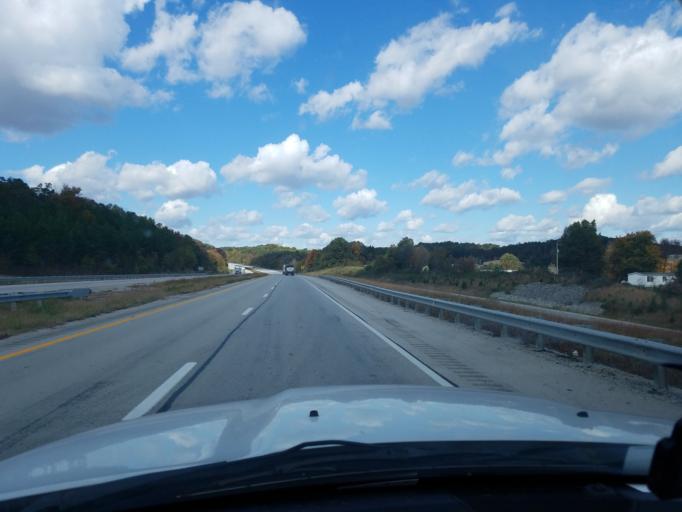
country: US
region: Kentucky
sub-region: Butler County
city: Morgantown
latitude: 37.2155
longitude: -86.7115
